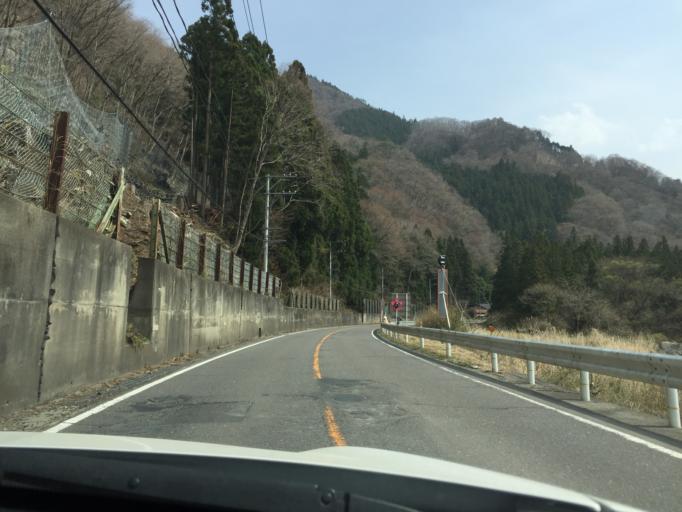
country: JP
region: Fukushima
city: Ishikawa
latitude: 37.0517
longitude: 140.6163
